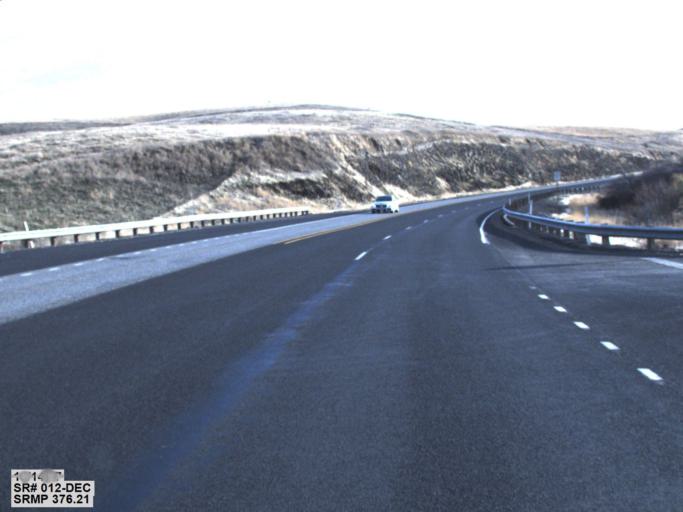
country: US
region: Washington
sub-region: Columbia County
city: Dayton
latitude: 46.4290
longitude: -117.9468
